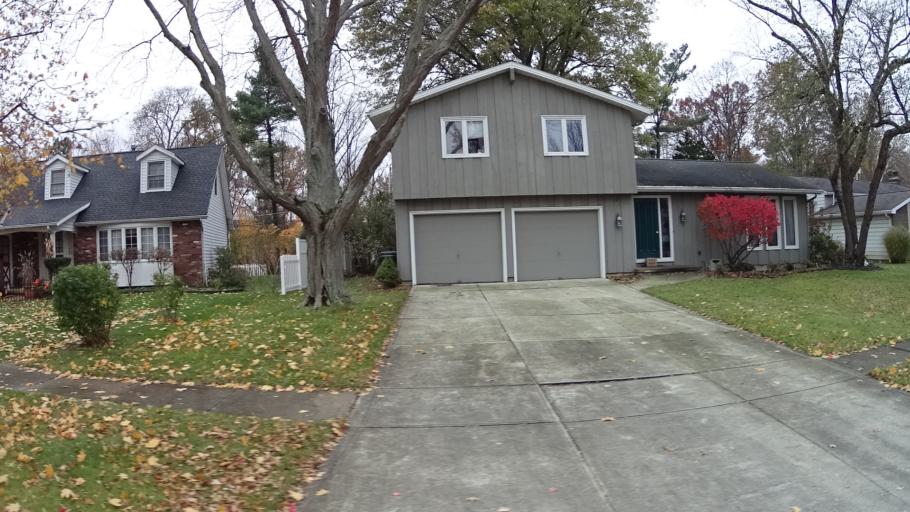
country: US
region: Ohio
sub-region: Lorain County
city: Sheffield
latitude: 41.4085
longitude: -82.0780
